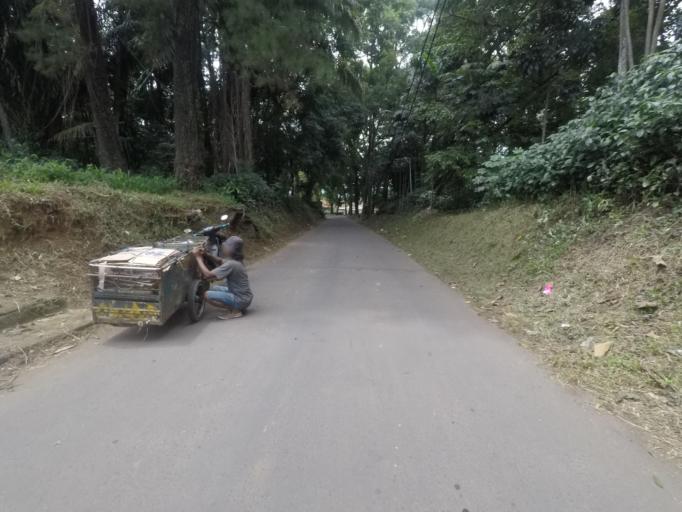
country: ID
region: West Java
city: Ciampea
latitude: -6.5494
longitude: 106.7466
